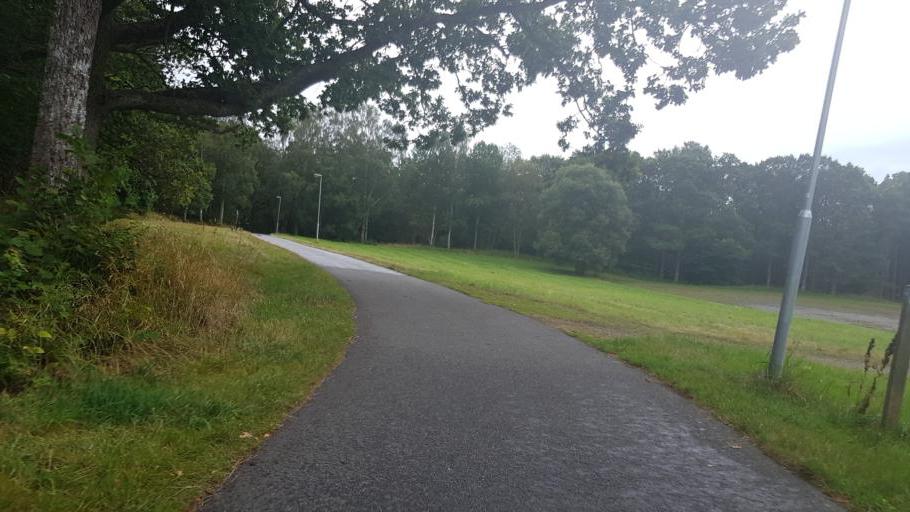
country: SE
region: Vaestra Goetaland
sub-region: Harryda Kommun
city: Molnlycke
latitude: 57.6619
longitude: 12.0981
